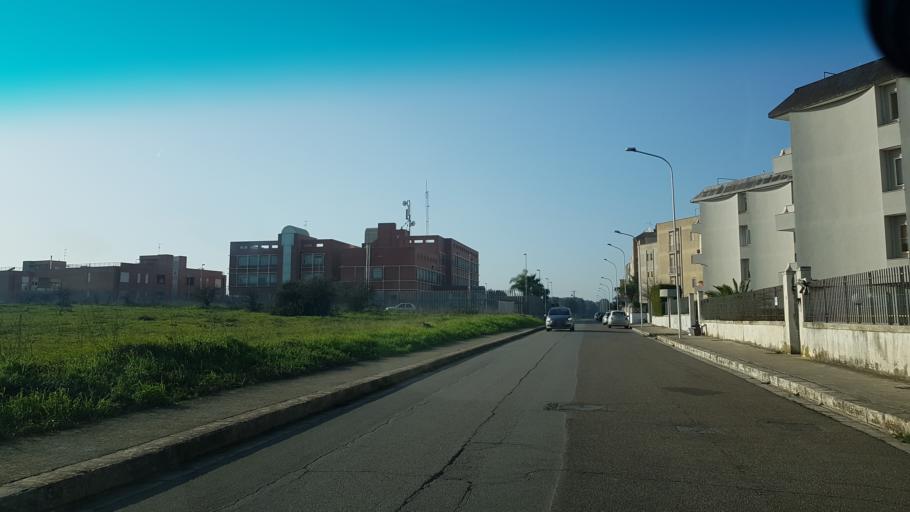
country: IT
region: Apulia
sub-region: Provincia di Brindisi
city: San Vito dei Normanni
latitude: 40.6622
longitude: 17.6962
